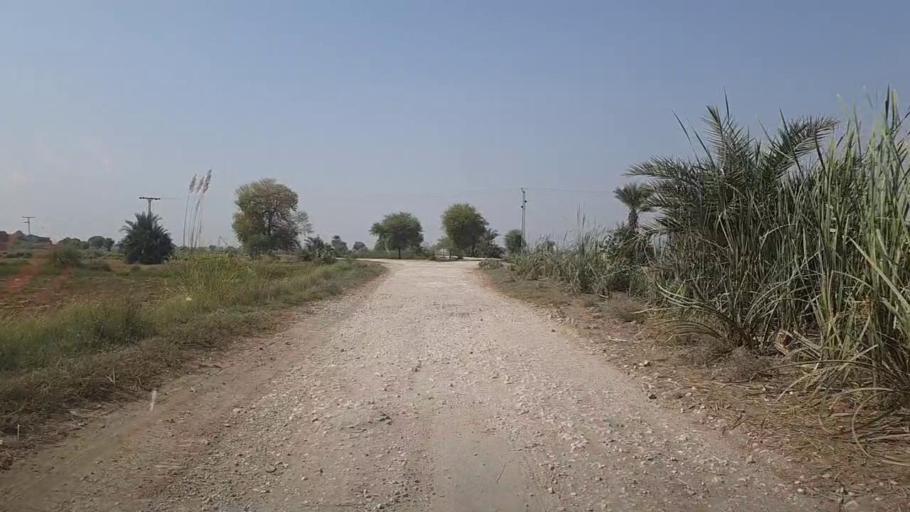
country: PK
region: Sindh
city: Kandhkot
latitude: 28.3884
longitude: 69.3239
